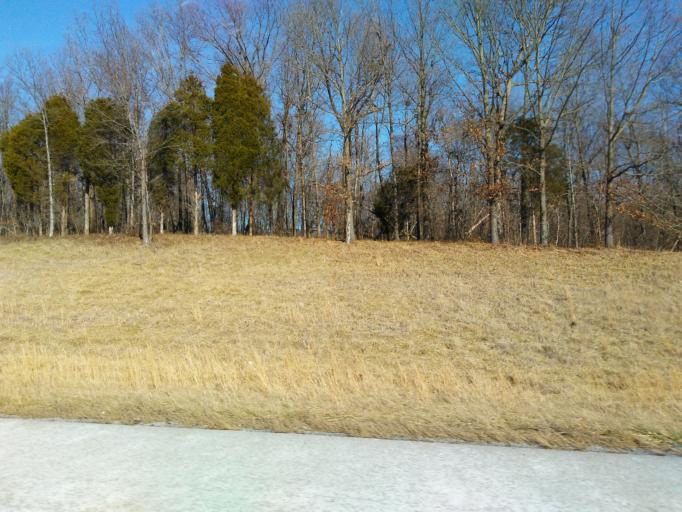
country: US
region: Illinois
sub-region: Massac County
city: Metropolis
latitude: 37.2068
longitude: -88.6947
